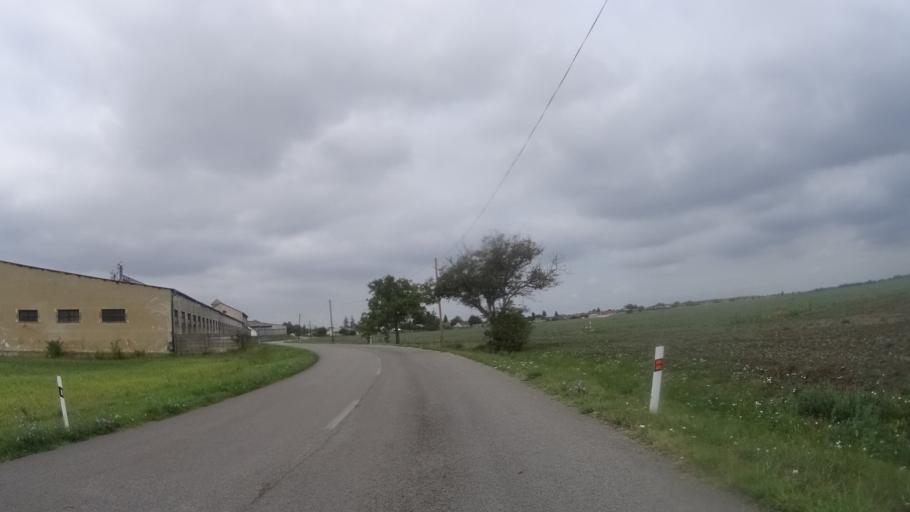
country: HU
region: Komarom-Esztergom
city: Acs
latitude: 47.7667
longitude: 17.9877
